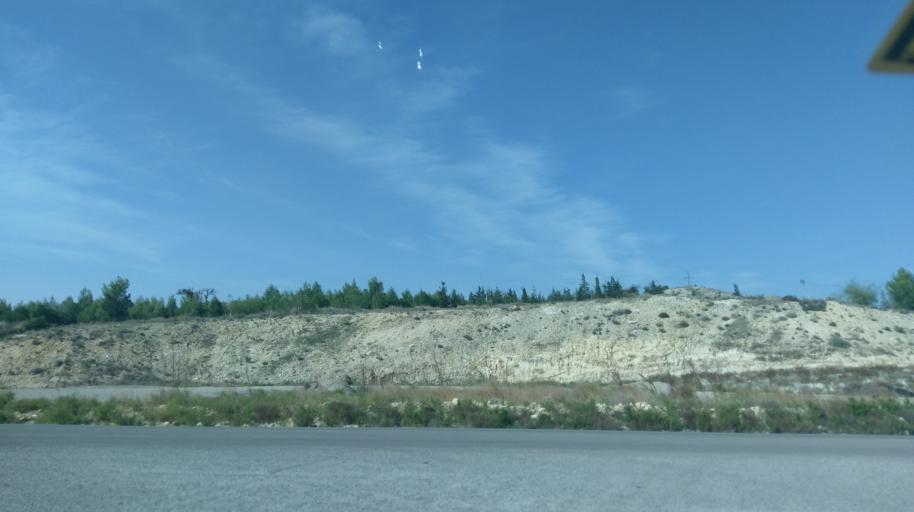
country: CY
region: Ammochostos
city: Trikomo
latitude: 35.3390
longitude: 33.9848
